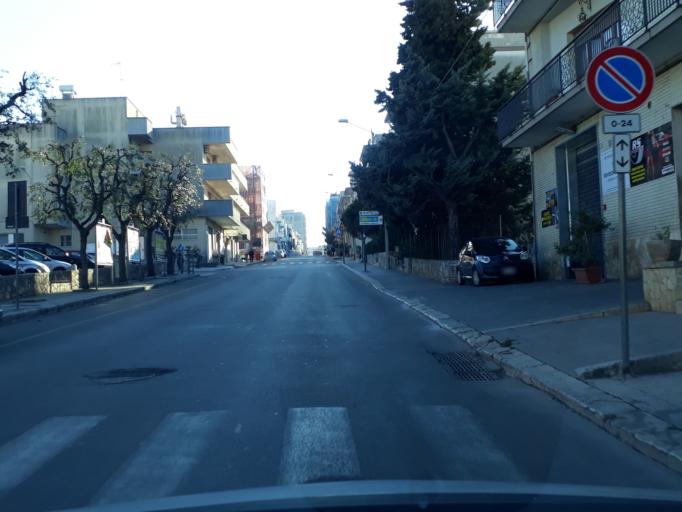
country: IT
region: Apulia
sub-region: Provincia di Bari
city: Locorotondo
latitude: 40.7595
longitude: 17.3285
